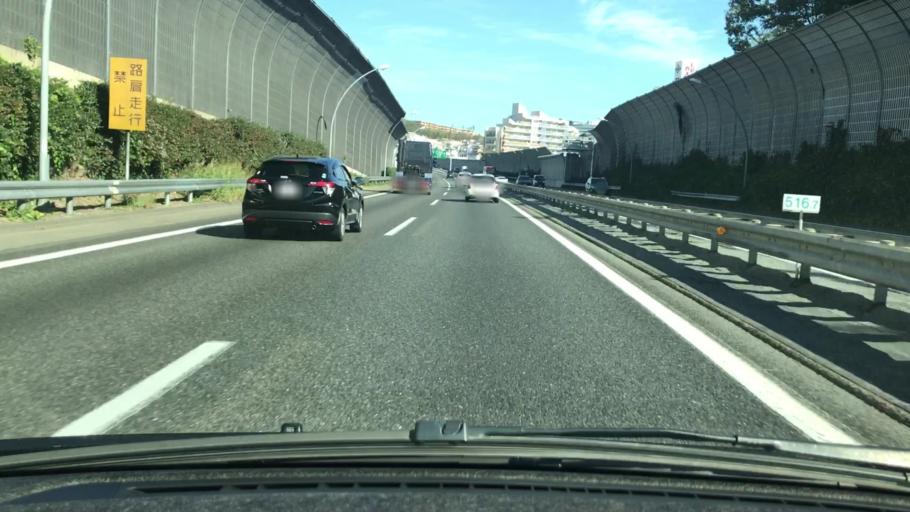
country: JP
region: Osaka
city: Suita
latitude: 34.7904
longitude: 135.5343
